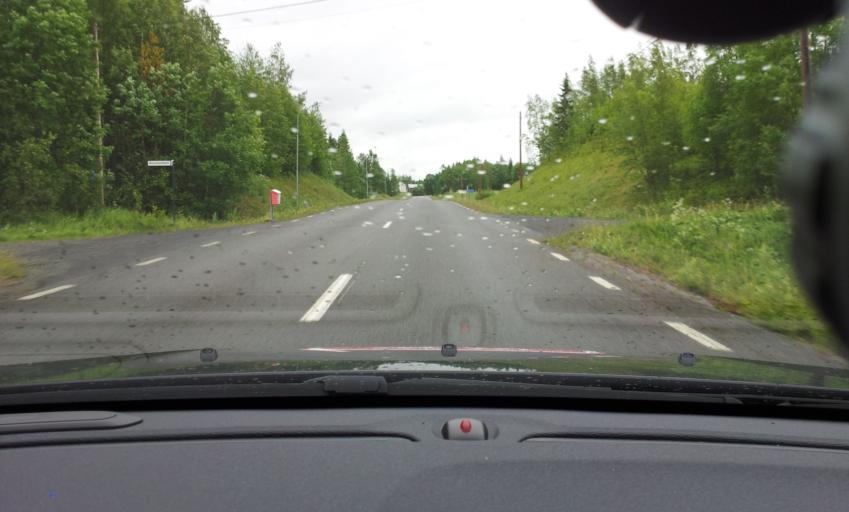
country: SE
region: Jaemtland
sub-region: OEstersunds Kommun
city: Lit
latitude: 63.6771
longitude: 15.0508
